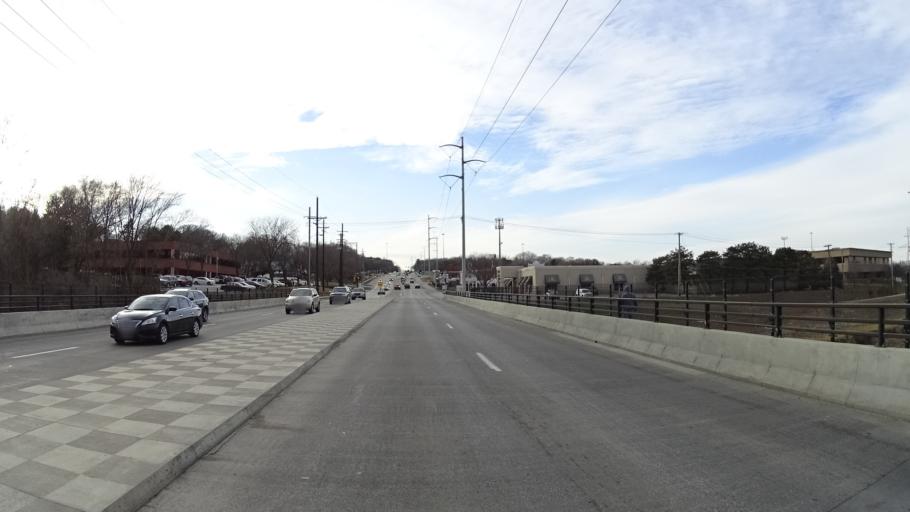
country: US
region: Nebraska
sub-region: Douglas County
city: Ralston
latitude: 41.2488
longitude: -96.0786
